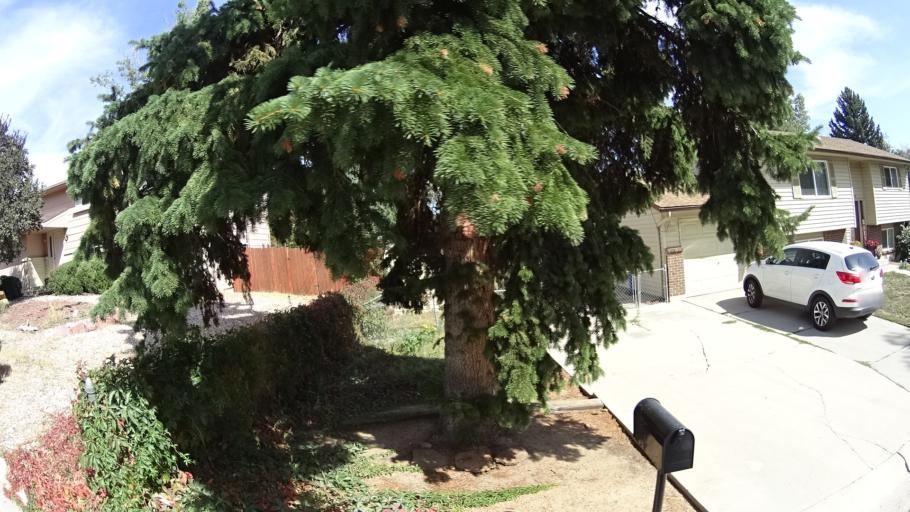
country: US
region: Colorado
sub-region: El Paso County
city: Cimarron Hills
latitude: 38.8923
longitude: -104.7691
